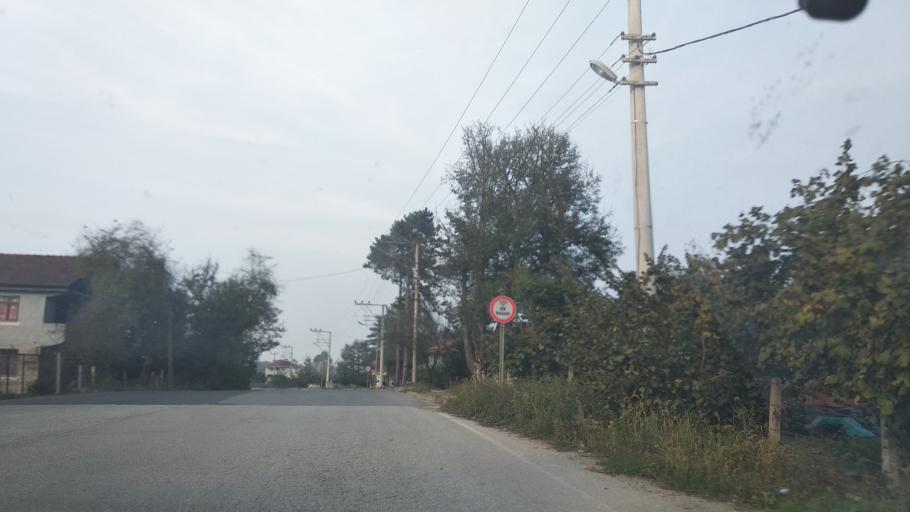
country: TR
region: Duzce
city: Duzce
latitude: 40.8083
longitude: 31.1785
